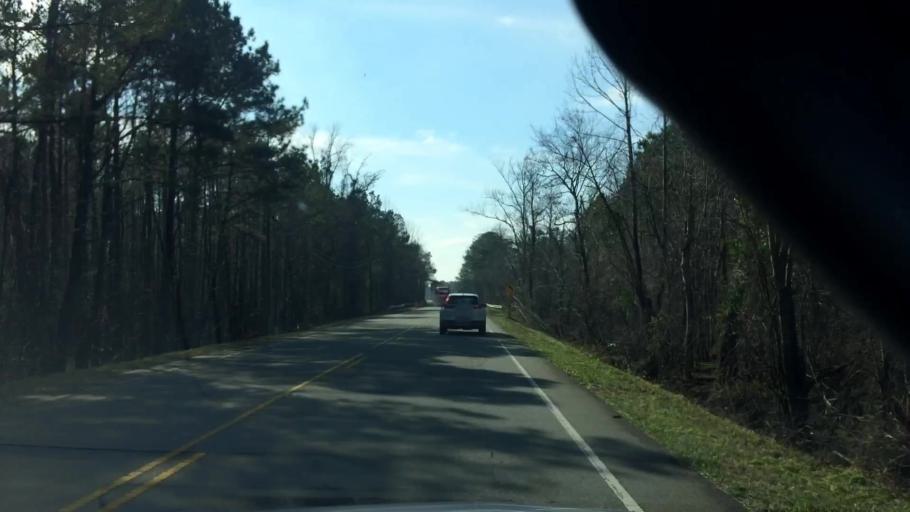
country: US
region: North Carolina
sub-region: Duplin County
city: Beulaville
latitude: 34.8287
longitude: -77.8357
